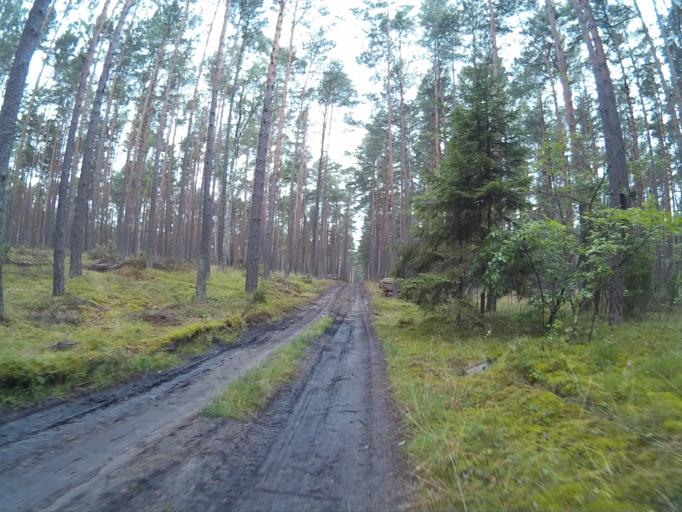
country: PL
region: Kujawsko-Pomorskie
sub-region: Powiat swiecki
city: Osie
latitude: 53.6773
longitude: 18.3581
